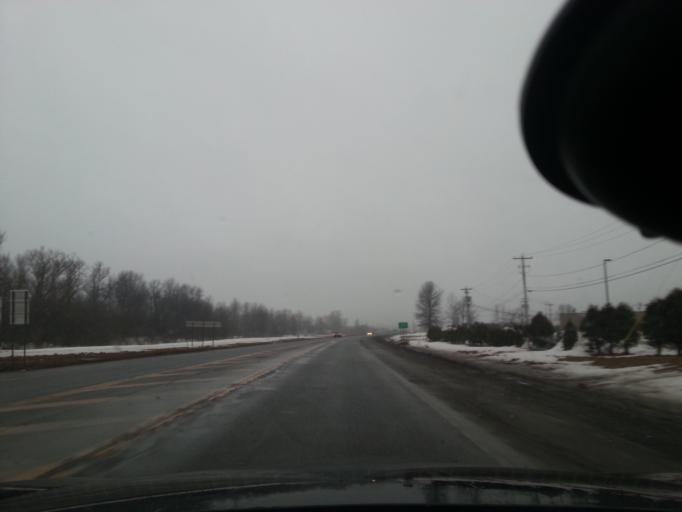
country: US
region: New York
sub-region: St. Lawrence County
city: Ogdensburg
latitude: 44.6893
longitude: -75.4764
